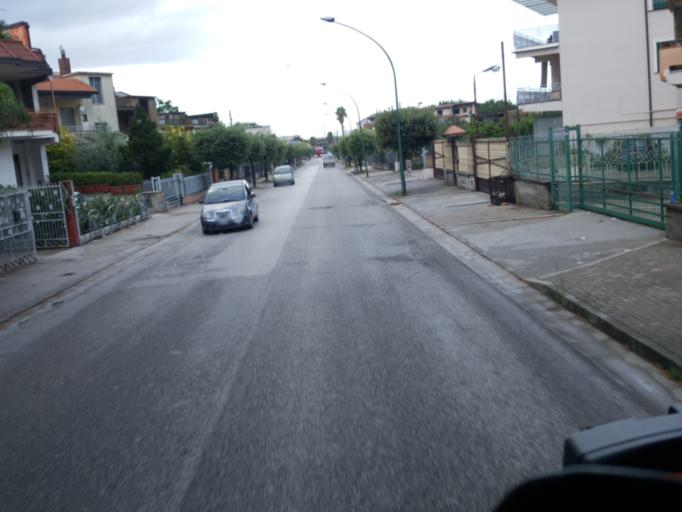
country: IT
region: Campania
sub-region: Provincia di Napoli
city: Palma Campania
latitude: 40.8570
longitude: 14.5528
